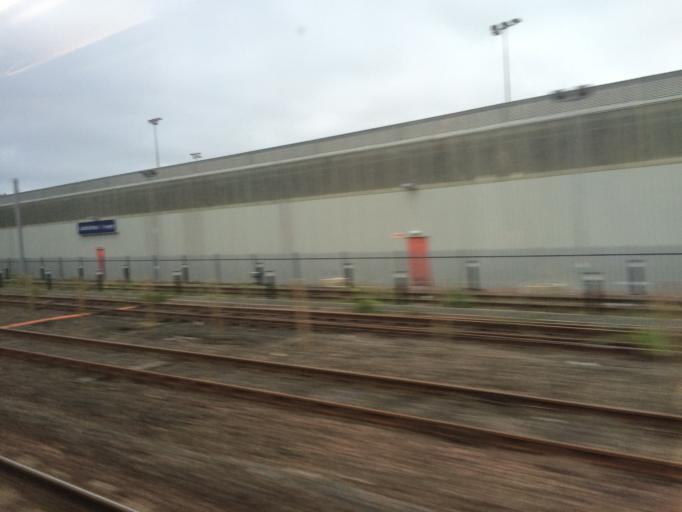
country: GB
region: Scotland
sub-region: East Dunbartonshire
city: Bishopbriggs
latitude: 55.8905
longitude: -4.2408
